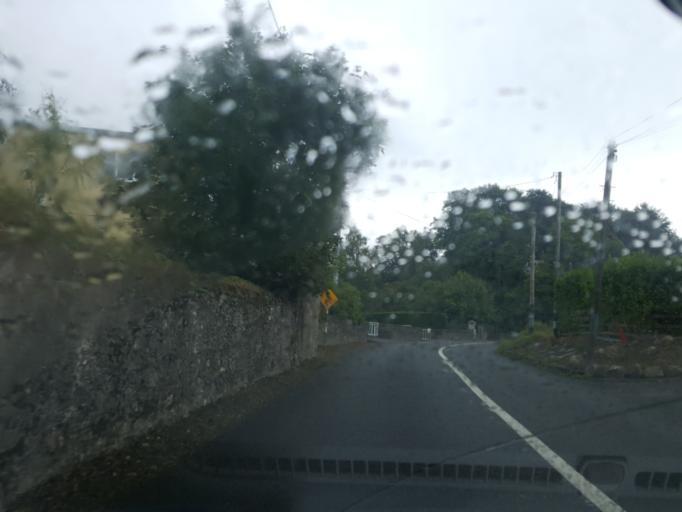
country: IE
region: Leinster
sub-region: Wicklow
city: Valleymount
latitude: 53.1323
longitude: -6.6089
